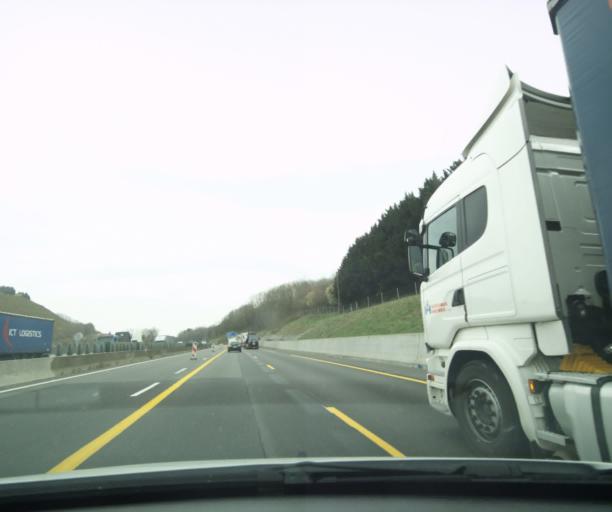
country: FR
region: Aquitaine
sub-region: Departement des Pyrenees-Atlantiques
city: Hendaye
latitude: 43.3409
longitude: -1.7400
